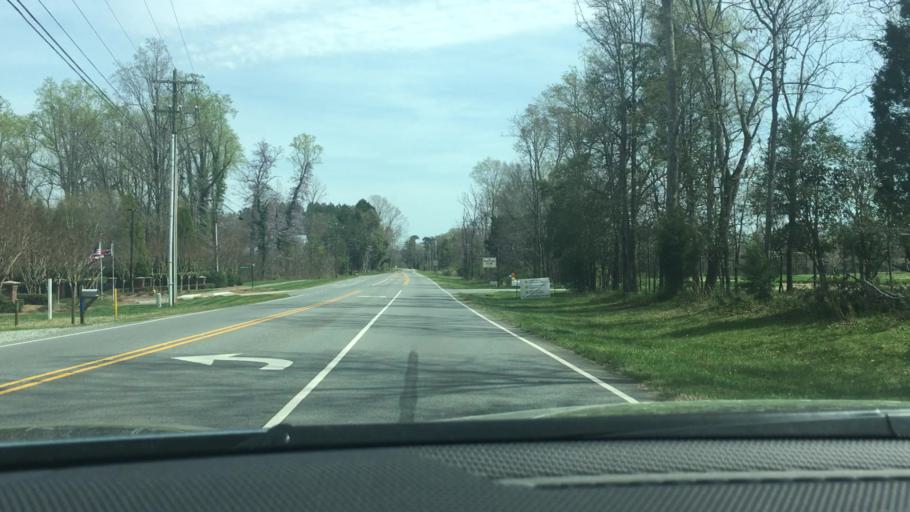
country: US
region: North Carolina
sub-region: Mecklenburg County
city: Huntersville
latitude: 35.4429
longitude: -80.7760
